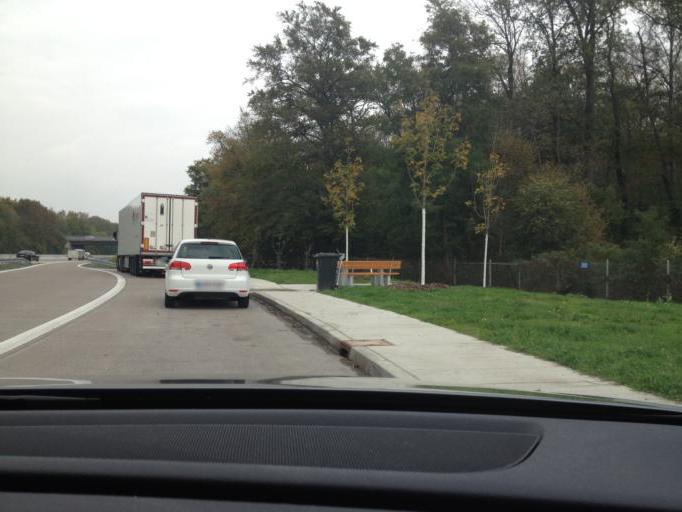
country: DE
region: Baden-Wuerttemberg
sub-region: Karlsruhe Region
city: Ketsch
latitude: 49.3720
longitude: 8.5452
